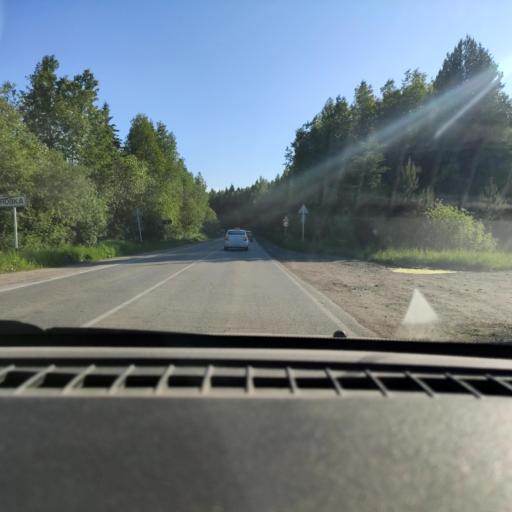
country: RU
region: Perm
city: Overyata
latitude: 58.1132
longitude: 55.8328
